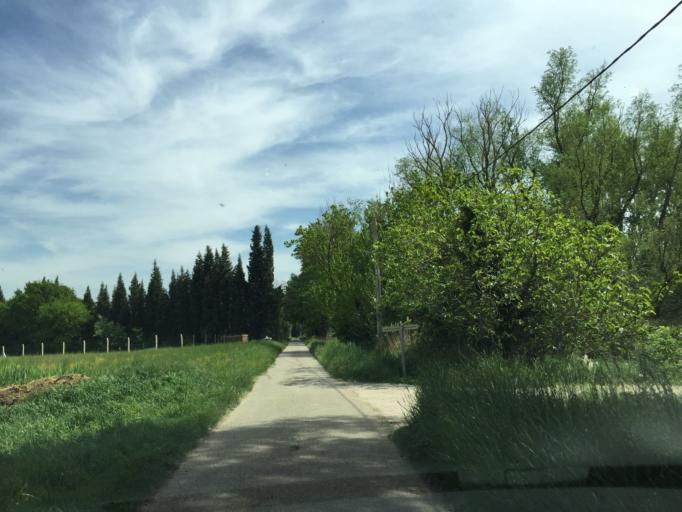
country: FR
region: Provence-Alpes-Cote d'Azur
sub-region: Departement du Vaucluse
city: Courthezon
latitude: 44.0880
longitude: 4.8601
